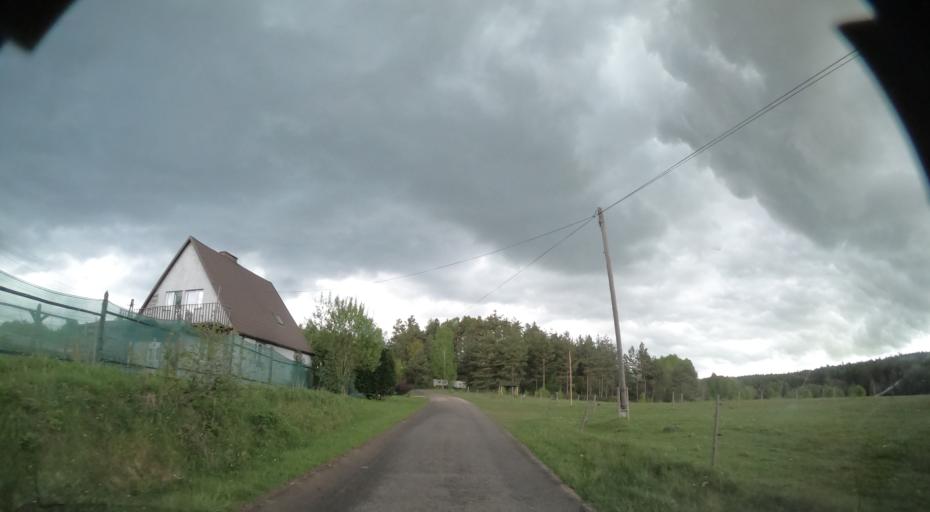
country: PL
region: West Pomeranian Voivodeship
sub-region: Powiat koszalinski
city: Polanow
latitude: 54.1172
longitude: 16.5013
